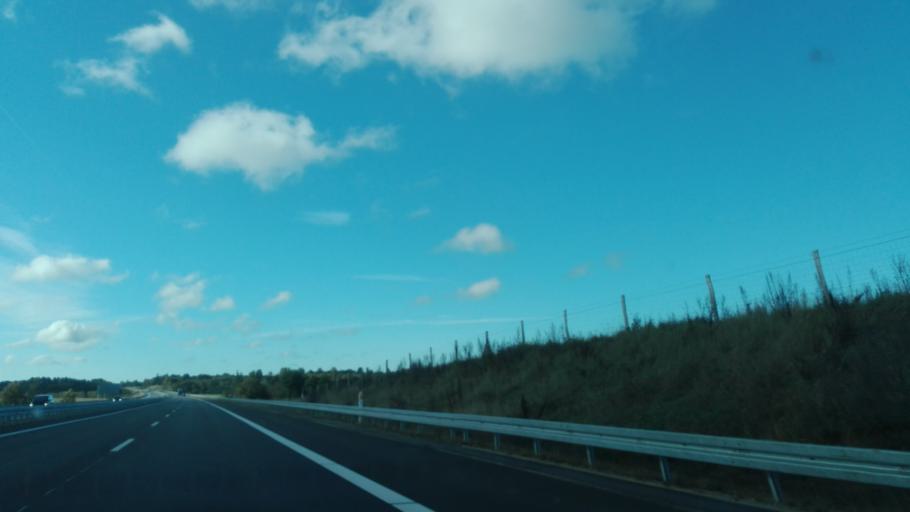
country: DK
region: Central Jutland
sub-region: Silkeborg Kommune
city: Silkeborg
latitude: 56.1895
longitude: 9.4941
